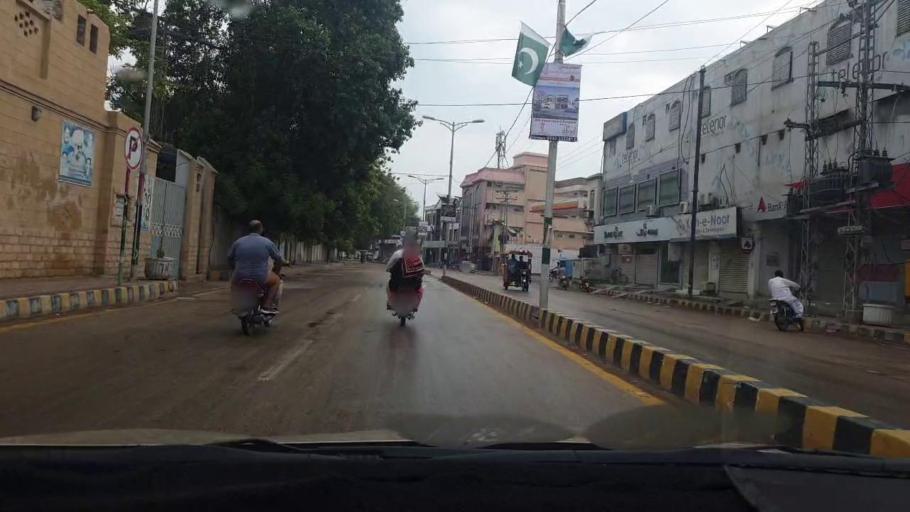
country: PK
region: Sindh
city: Larkana
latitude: 27.5556
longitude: 68.2086
